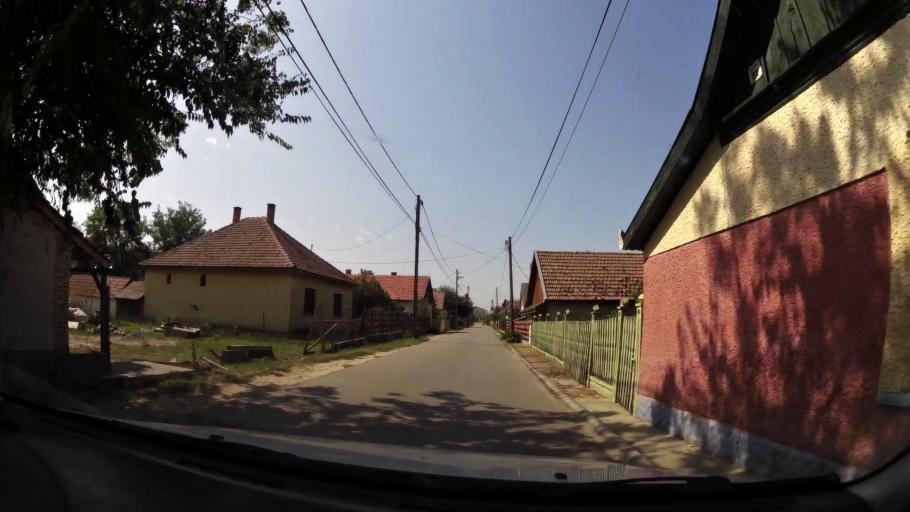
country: HU
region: Pest
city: Ujszilvas
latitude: 47.2707
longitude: 19.9197
